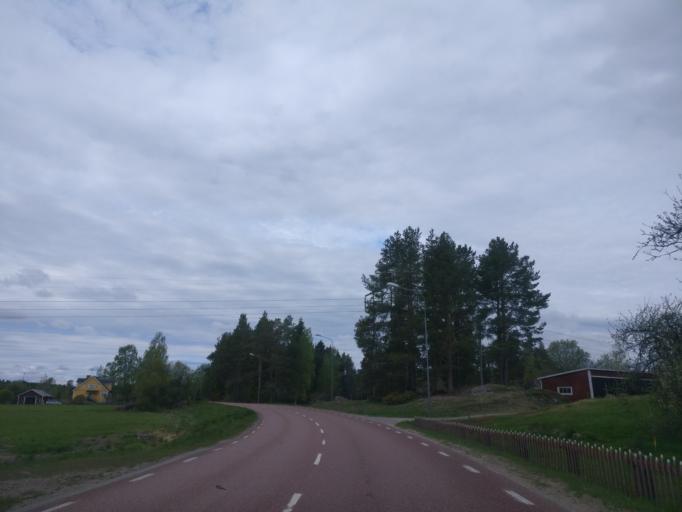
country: SE
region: Gaevleborg
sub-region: Soderhamns Kommun
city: Soderhamn
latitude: 61.3663
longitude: 16.9435
